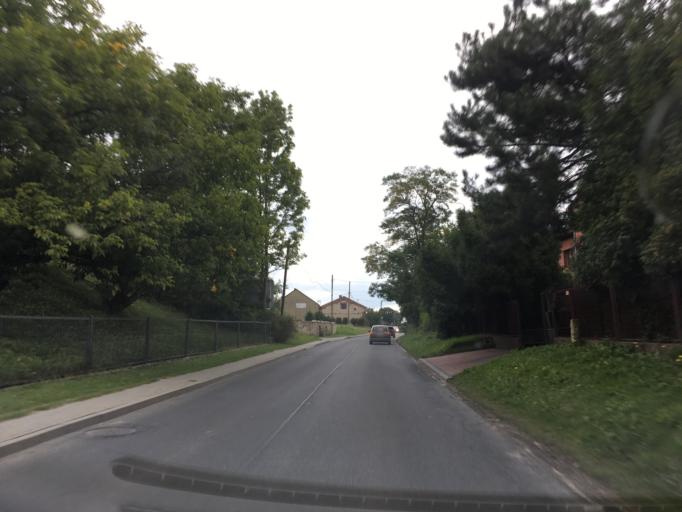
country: PL
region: Lesser Poland Voivodeship
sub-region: Powiat olkuski
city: Wolbrom
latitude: 50.3901
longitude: 19.7613
